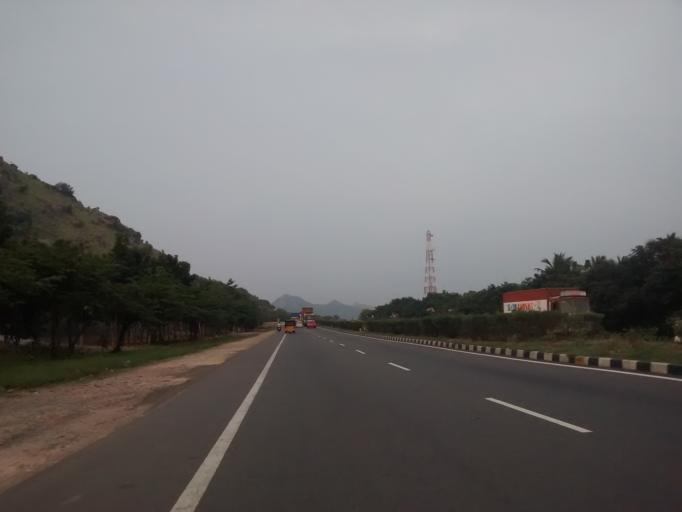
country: IN
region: Tamil Nadu
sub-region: Krishnagiri
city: Kaverippattanam
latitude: 12.3273
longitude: 78.2107
